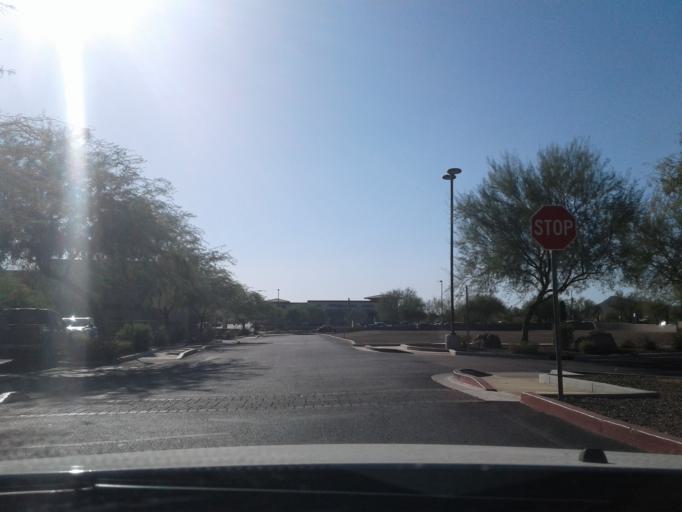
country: US
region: Arizona
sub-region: Maricopa County
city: Anthem
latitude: 33.7976
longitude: -112.1167
